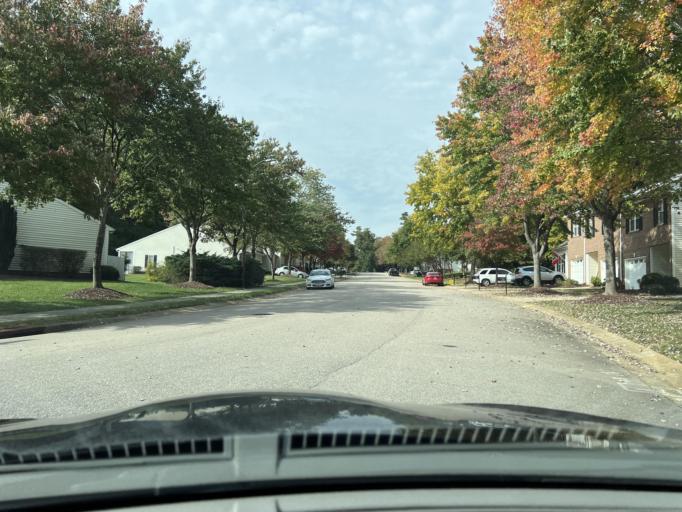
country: US
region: North Carolina
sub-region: Wake County
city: Wake Forest
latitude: 35.8898
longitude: -78.5912
